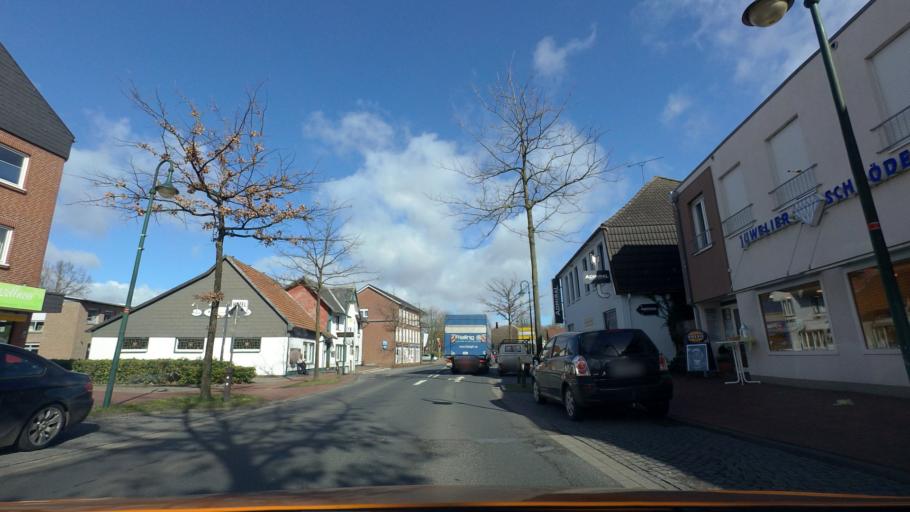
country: DE
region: Lower Saxony
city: Edewecht
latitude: 53.1274
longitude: 7.9838
